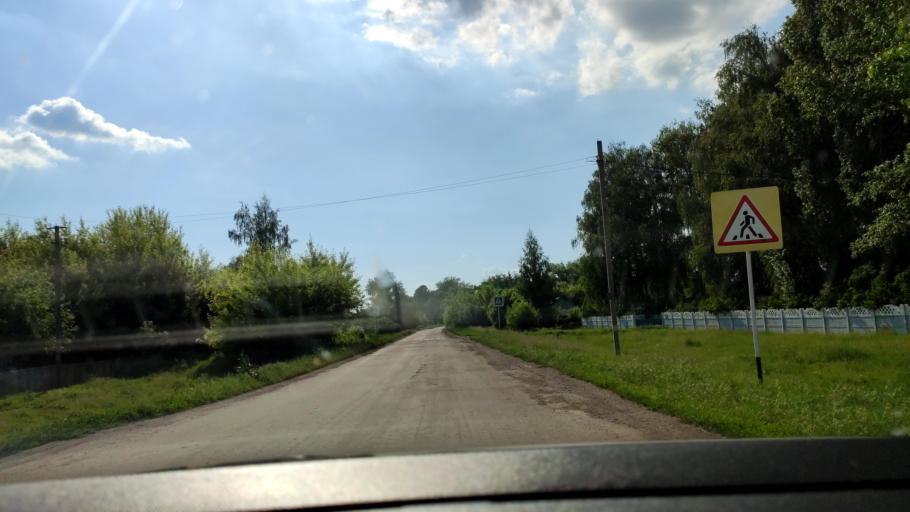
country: RU
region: Voronezj
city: Panino
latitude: 51.6099
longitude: 40.0597
